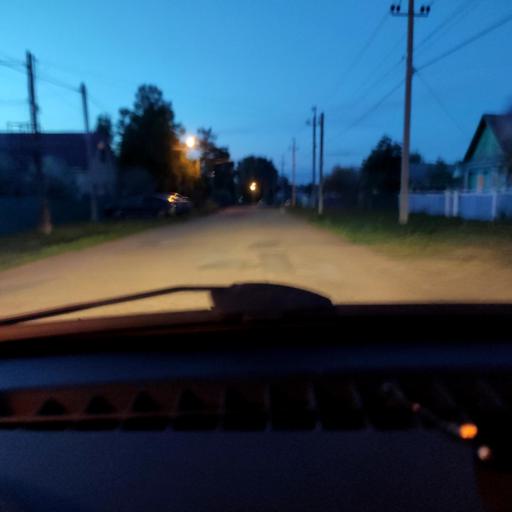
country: RU
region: Bashkortostan
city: Karmaskaly
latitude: 54.3695
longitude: 56.1638
